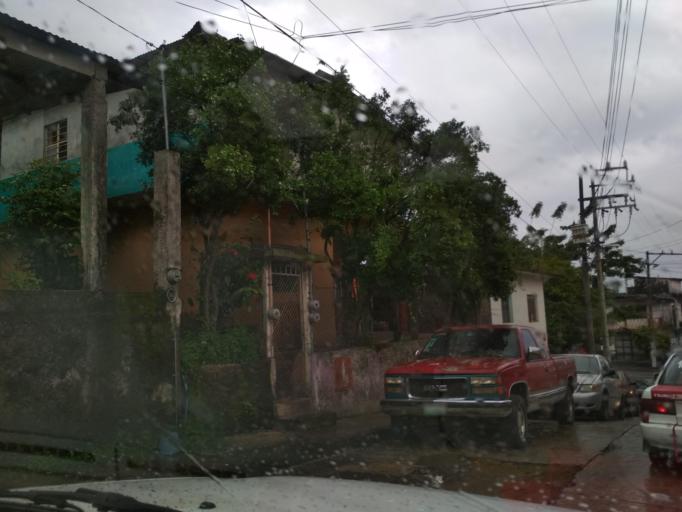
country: MX
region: Veracruz
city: San Andres Tuxtla
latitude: 18.4551
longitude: -95.2153
